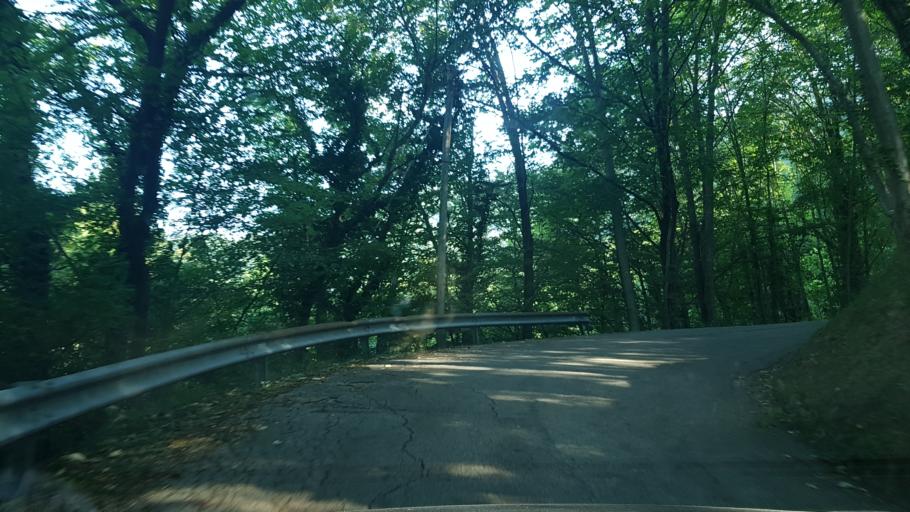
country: IT
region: Friuli Venezia Giulia
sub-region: Provincia di Udine
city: Nimis
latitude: 46.2264
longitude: 13.2478
